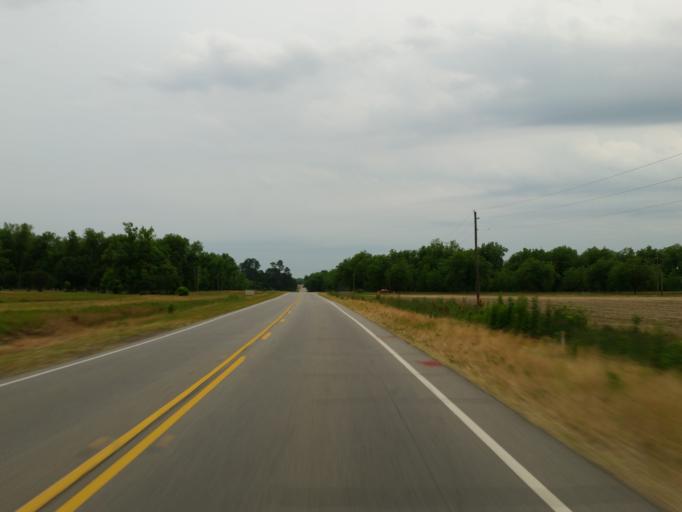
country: US
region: Georgia
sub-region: Dooly County
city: Vienna
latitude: 32.0480
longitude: -83.7966
